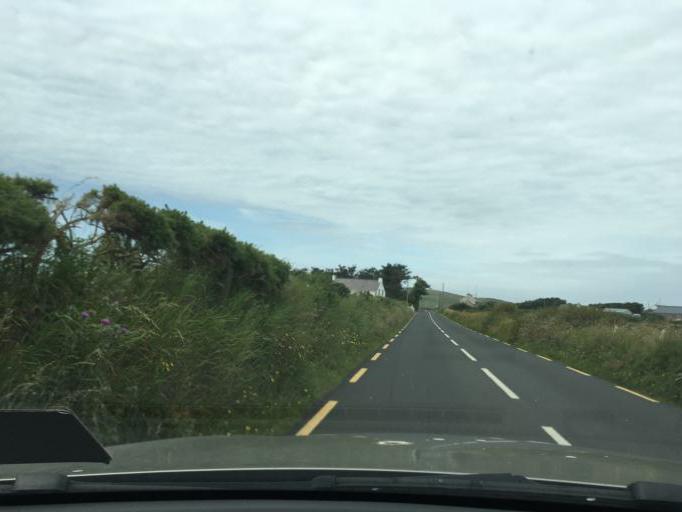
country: IE
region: Ulster
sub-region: County Donegal
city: Carndonagh
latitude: 55.3564
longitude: -7.3289
